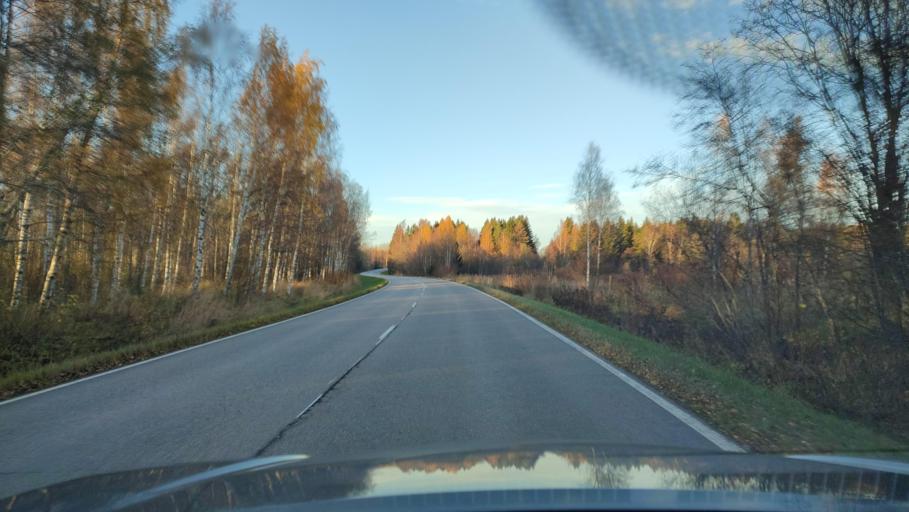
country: FI
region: Ostrobothnia
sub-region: Sydosterbotten
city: Kristinestad
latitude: 62.2843
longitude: 21.3783
